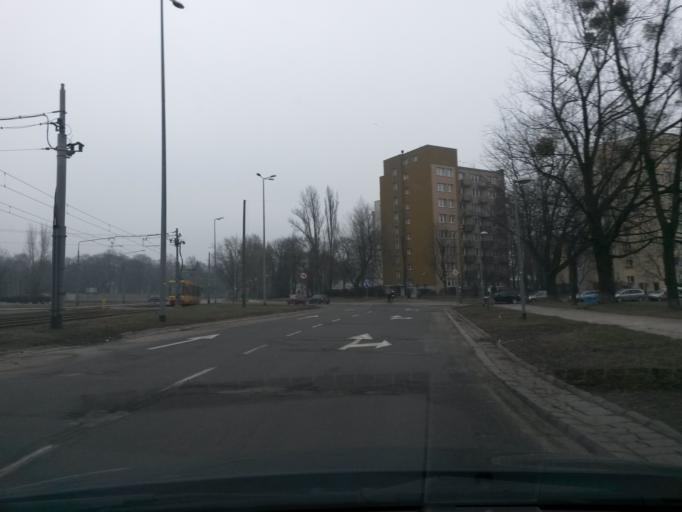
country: PL
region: Masovian Voivodeship
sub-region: Warszawa
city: Wola
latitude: 52.2441
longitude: 20.9664
